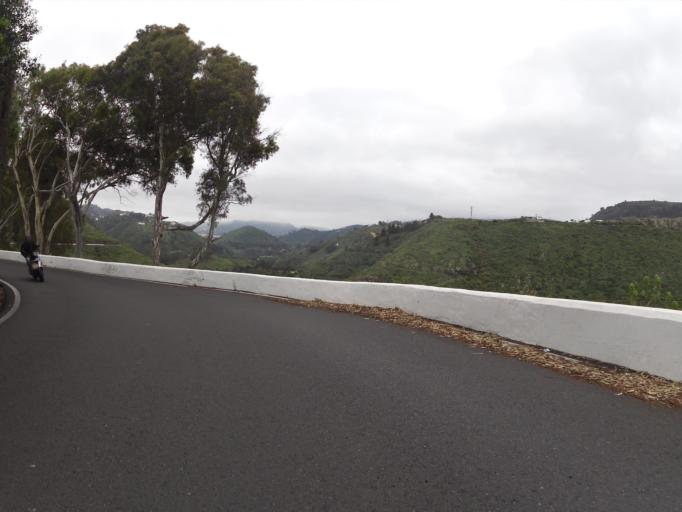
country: ES
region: Canary Islands
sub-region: Provincia de Las Palmas
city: Arucas
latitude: 28.0866
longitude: -15.5106
